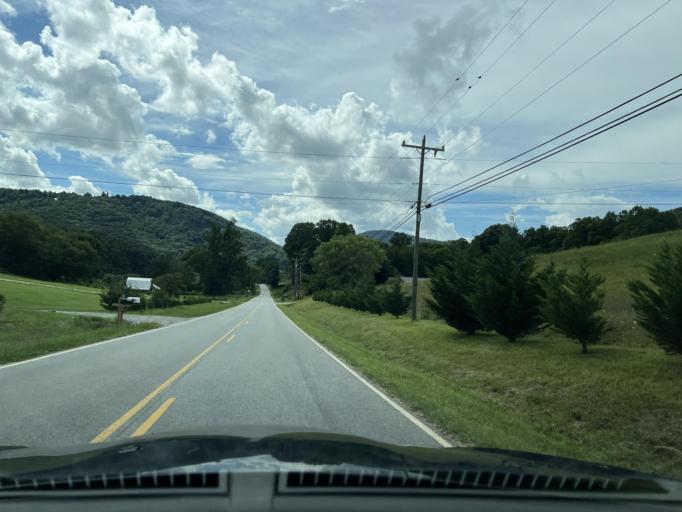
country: US
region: North Carolina
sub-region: Henderson County
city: Fruitland
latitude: 35.3973
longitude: -82.3953
